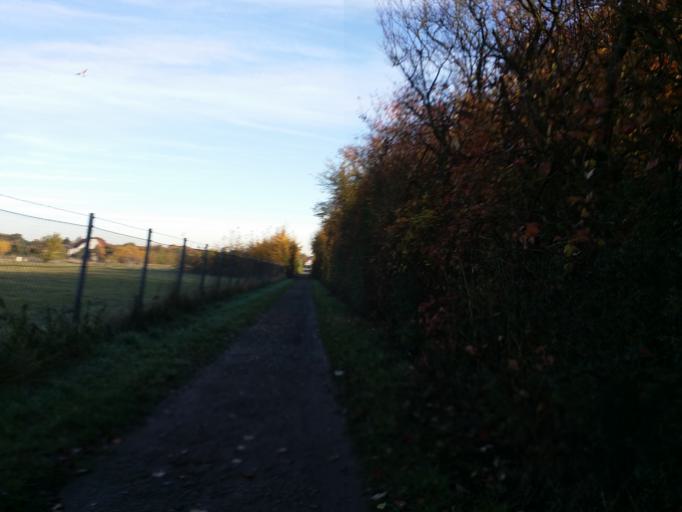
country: DE
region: Bremen
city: Bremen
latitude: 53.0458
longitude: 8.8142
